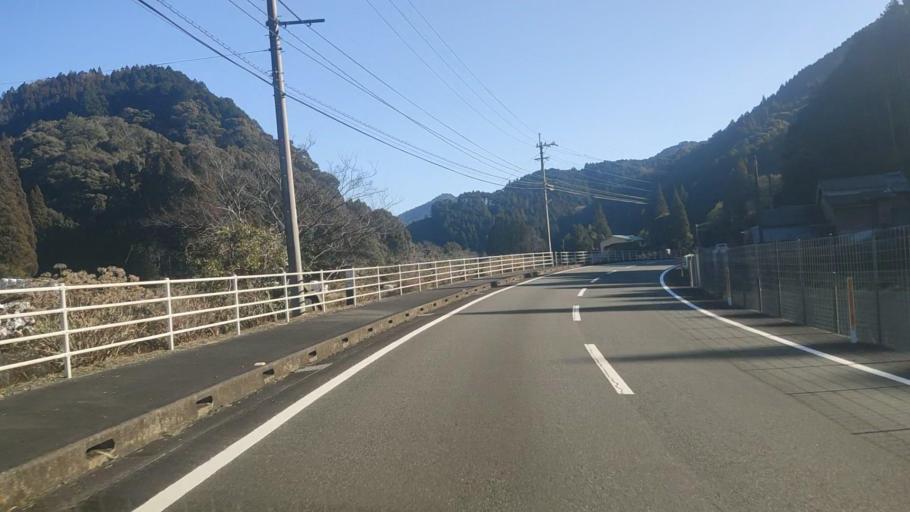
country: JP
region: Oita
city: Saiki
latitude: 32.7711
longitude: 131.8076
